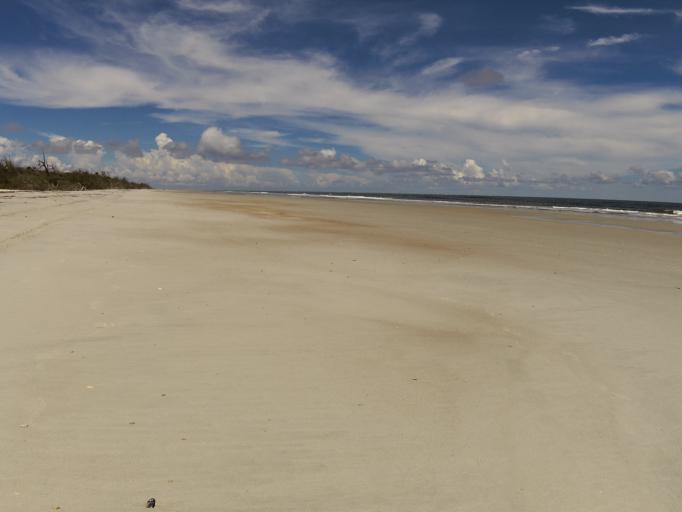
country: US
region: Florida
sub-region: Duval County
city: Atlantic Beach
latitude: 30.4713
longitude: -81.4127
